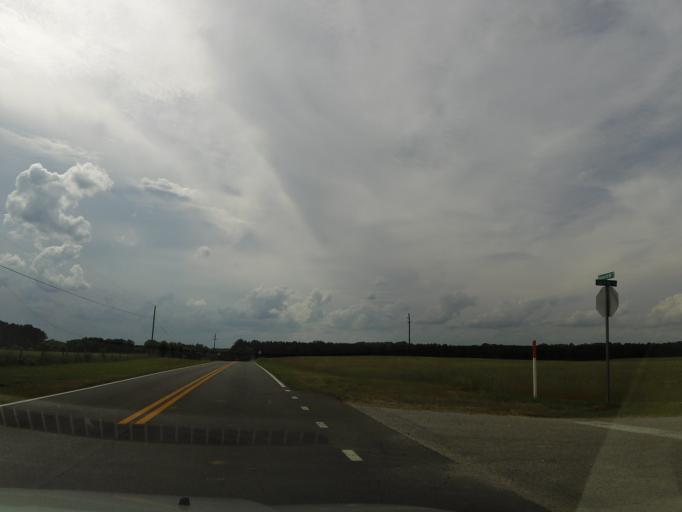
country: US
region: Georgia
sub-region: McDuffie County
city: Thomson
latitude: 33.5278
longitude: -82.4756
